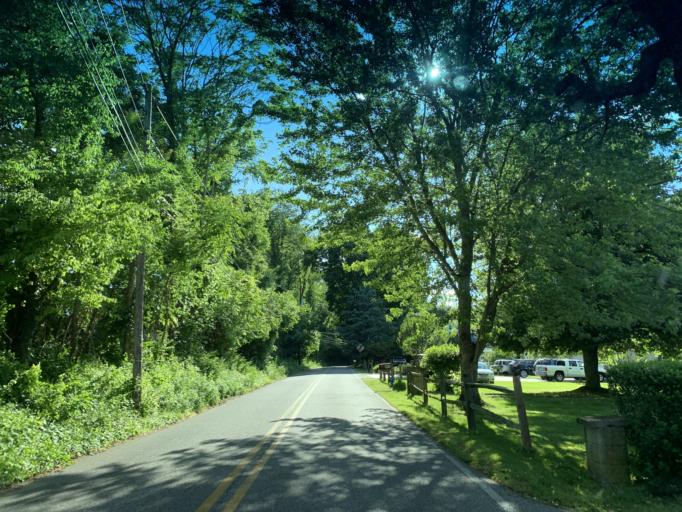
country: US
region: Maryland
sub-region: Cecil County
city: Perryville
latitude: 39.5735
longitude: -76.0759
